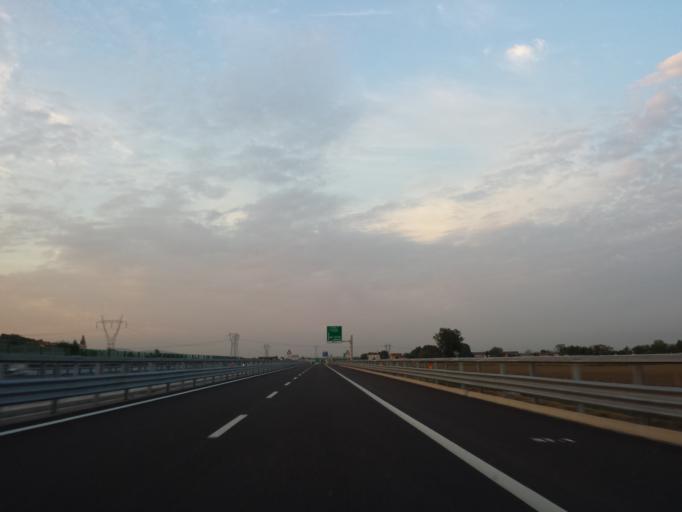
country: IT
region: Veneto
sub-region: Provincia di Vicenza
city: Albettone
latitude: 45.3730
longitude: 11.6103
